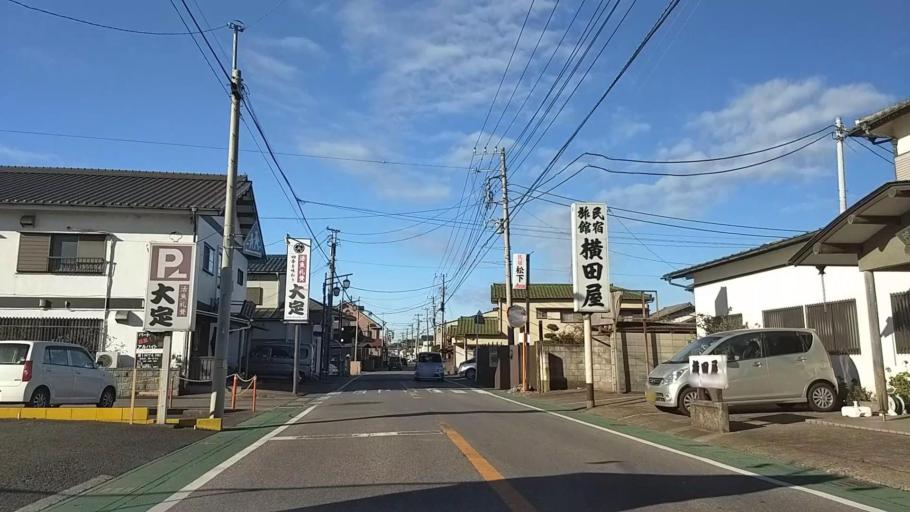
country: JP
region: Chiba
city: Futtsu
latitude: 35.3133
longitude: 139.8161
